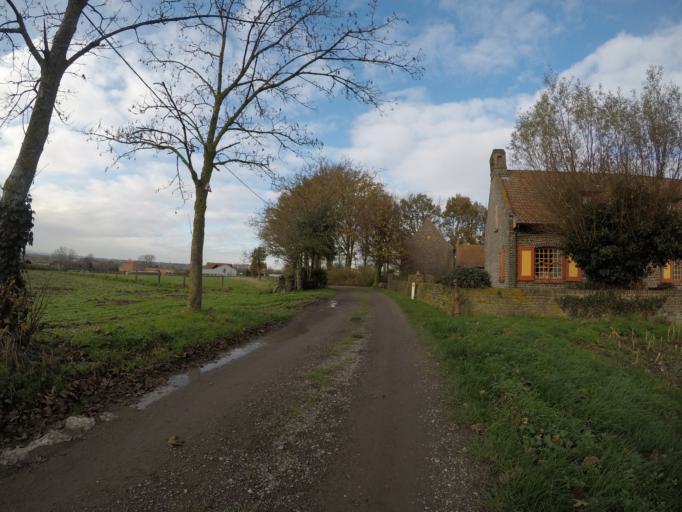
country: BE
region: Flanders
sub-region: Provincie West-Vlaanderen
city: Wervik
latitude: 50.8073
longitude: 3.0116
